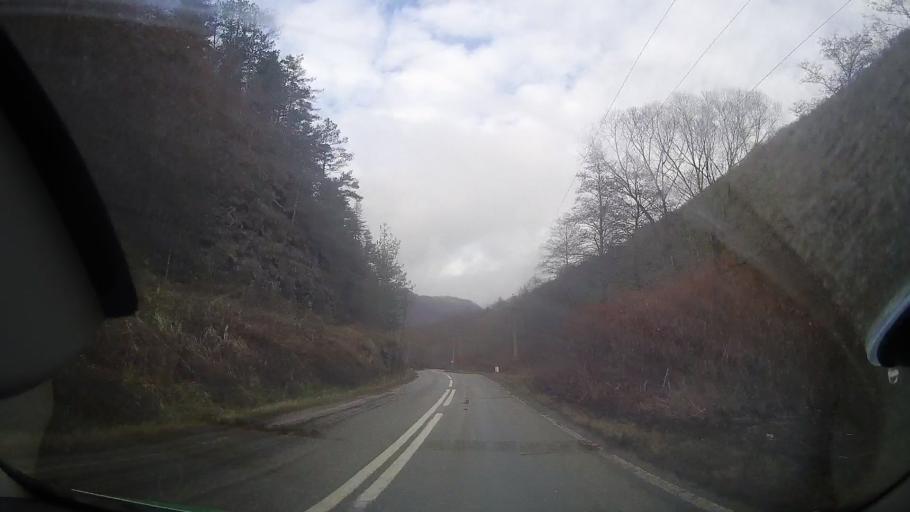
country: RO
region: Alba
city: Salciua de Sus
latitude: 46.4286
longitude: 23.4631
